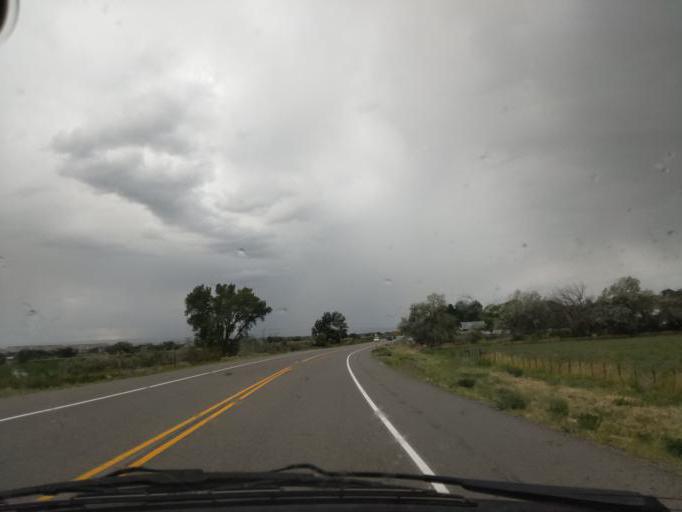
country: US
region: Colorado
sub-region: Delta County
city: Orchard City
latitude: 38.7817
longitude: -107.9441
